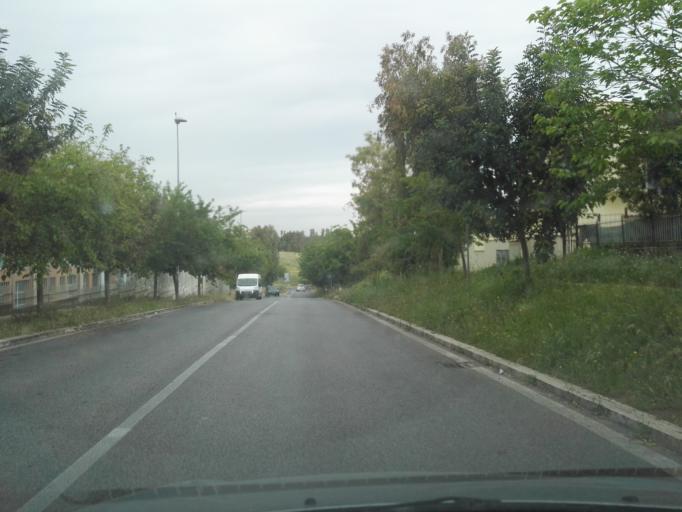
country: IT
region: Latium
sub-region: Citta metropolitana di Roma Capitale
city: Selcetta
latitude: 41.7675
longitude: 12.4703
